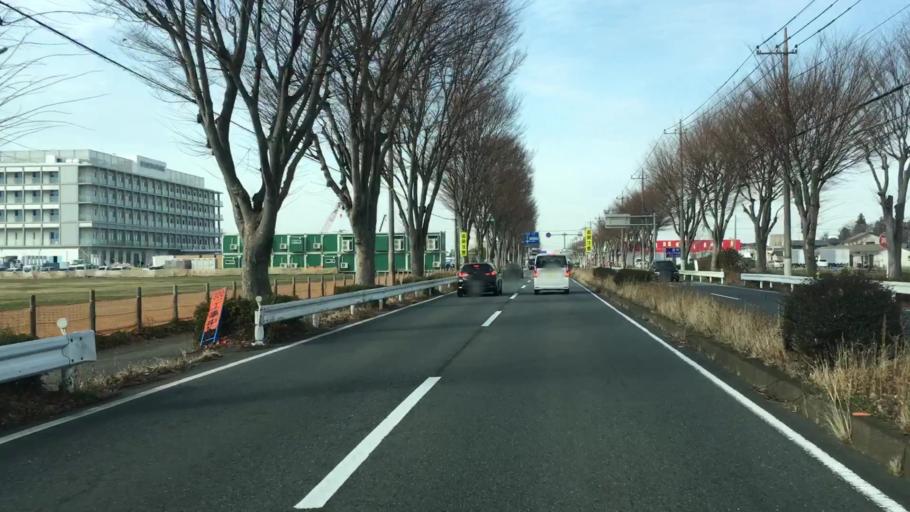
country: JP
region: Gunma
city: Tatebayashi
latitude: 36.2315
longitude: 139.5542
